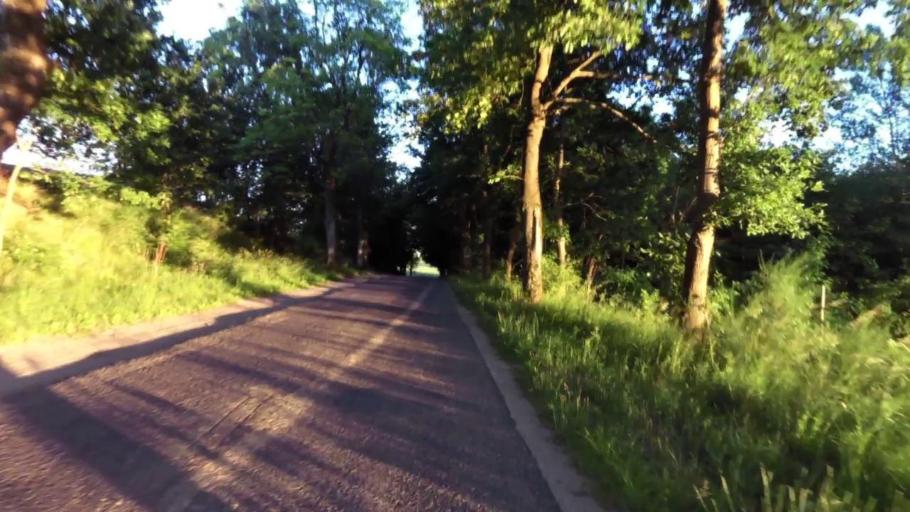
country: PL
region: West Pomeranian Voivodeship
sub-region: Powiat bialogardzki
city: Bialogard
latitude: 54.0396
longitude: 16.0469
